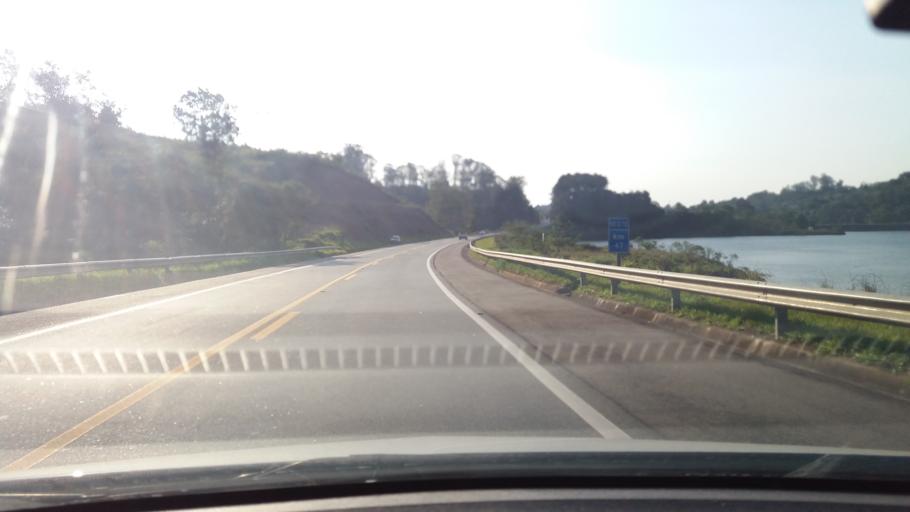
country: BR
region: Sao Paulo
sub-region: Franco Da Rocha
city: Franco da Rocha
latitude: -23.3341
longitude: -46.6734
